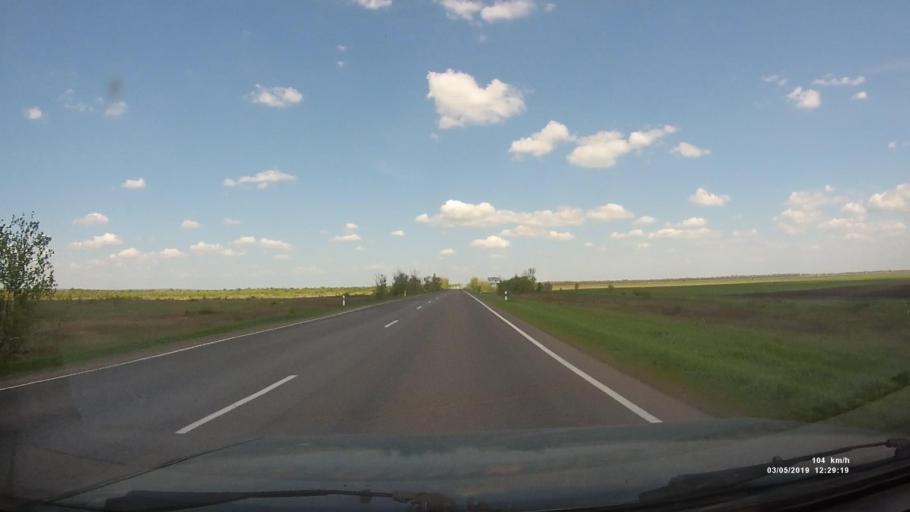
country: RU
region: Rostov
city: Semikarakorsk
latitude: 47.4858
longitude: 40.7348
